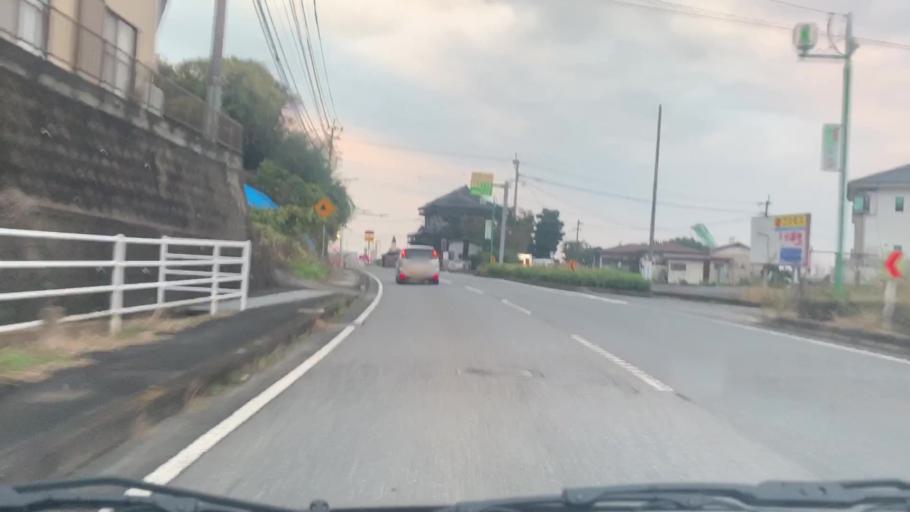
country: JP
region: Saga Prefecture
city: Ureshinomachi-shimojuku
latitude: 33.0380
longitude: 129.9220
